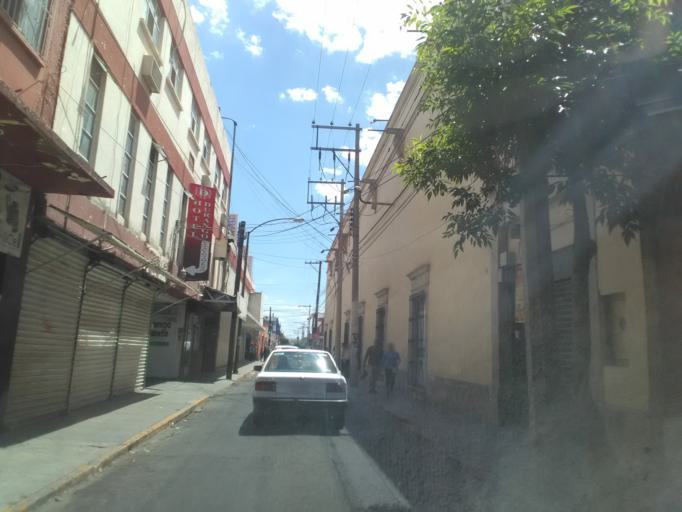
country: MX
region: Durango
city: Victoria de Durango
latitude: 24.0247
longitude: -104.6649
